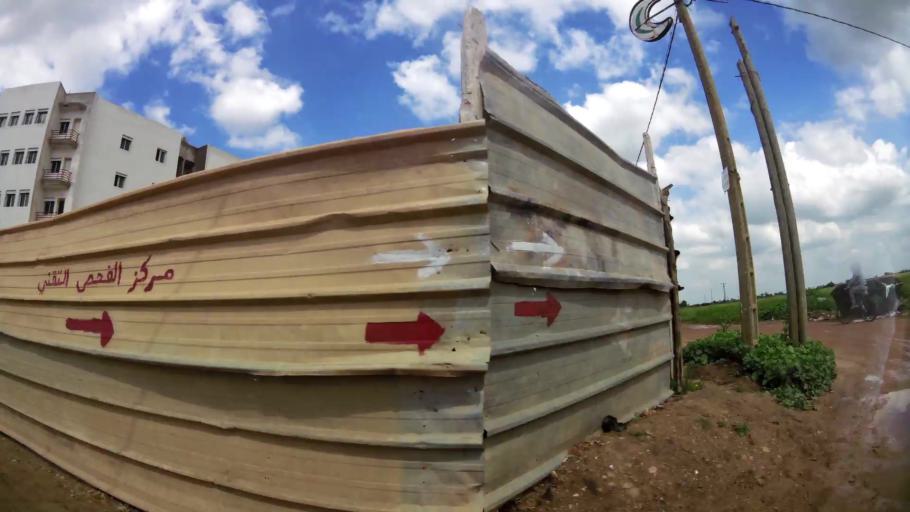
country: MA
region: Chaouia-Ouardigha
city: Nouaseur
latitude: 33.3619
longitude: -7.5365
